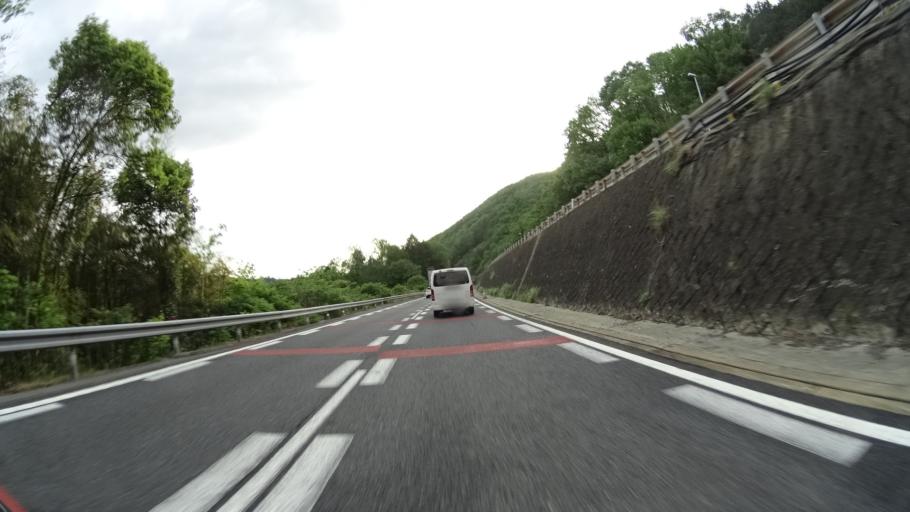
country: JP
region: Gifu
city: Nakatsugawa
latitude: 35.5116
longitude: 137.5592
